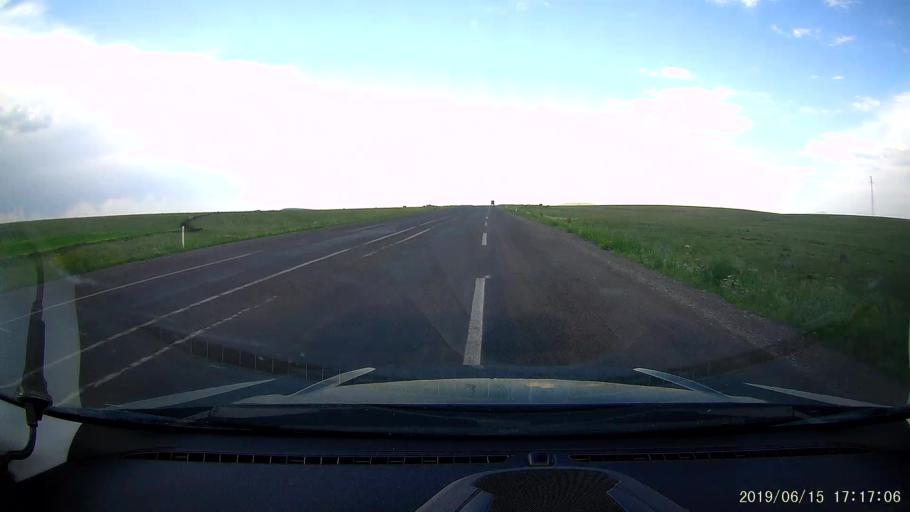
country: TR
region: Kars
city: Kars
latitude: 40.6144
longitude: 43.2315
